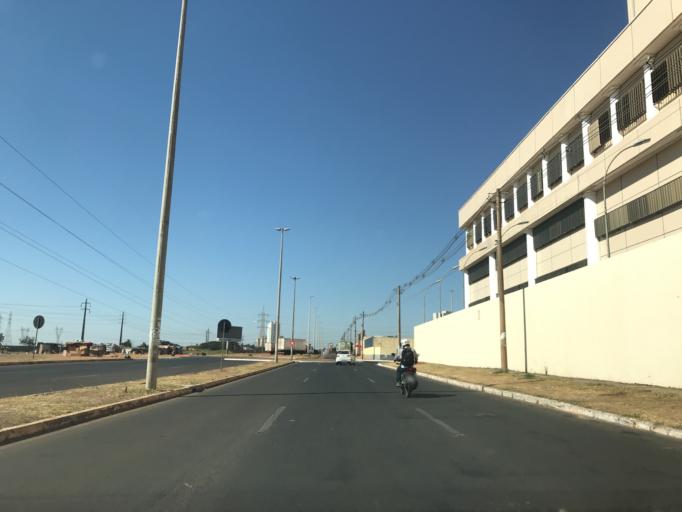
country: BR
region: Federal District
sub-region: Brasilia
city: Brasilia
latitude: -15.8464
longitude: -48.0398
